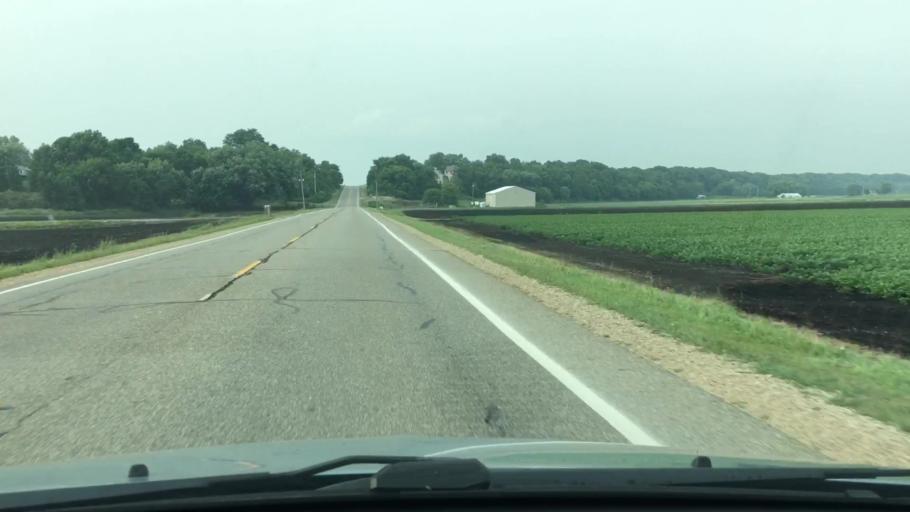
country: US
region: Michigan
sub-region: Ottawa County
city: Hudsonville
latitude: 42.8606
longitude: -85.9007
